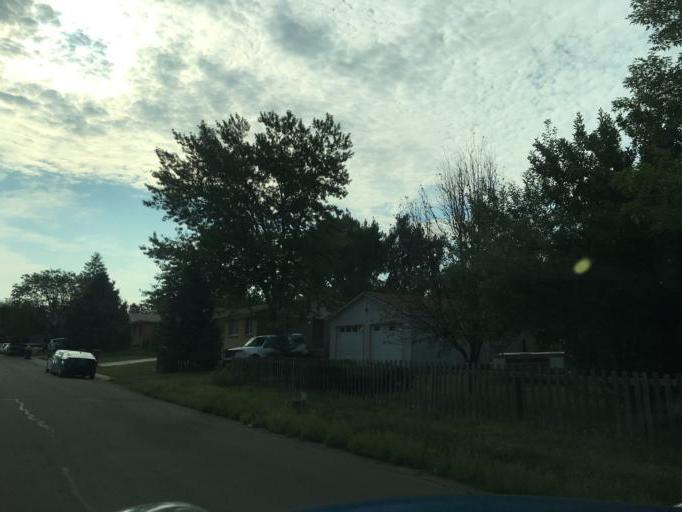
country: US
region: Colorado
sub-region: Jefferson County
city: Wheat Ridge
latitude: 39.7539
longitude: -105.1065
